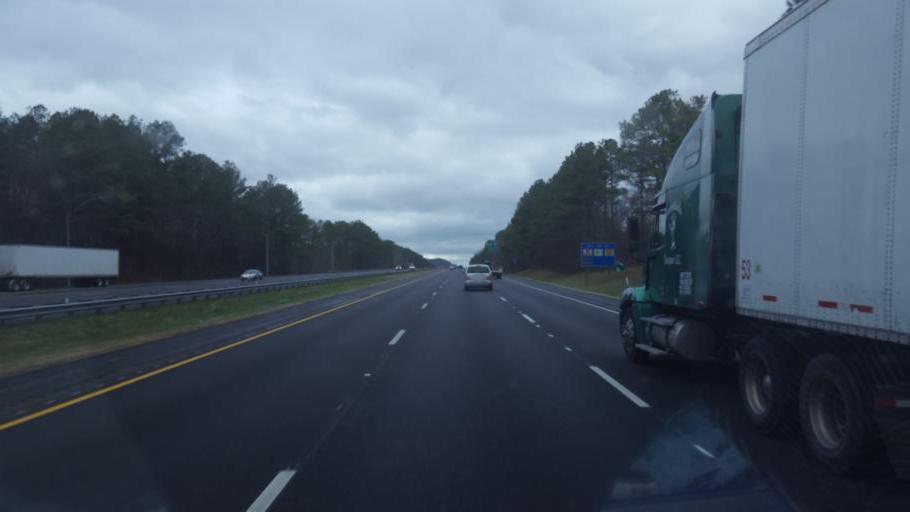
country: US
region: Georgia
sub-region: Catoosa County
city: Ringgold
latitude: 34.8831
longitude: -85.0557
